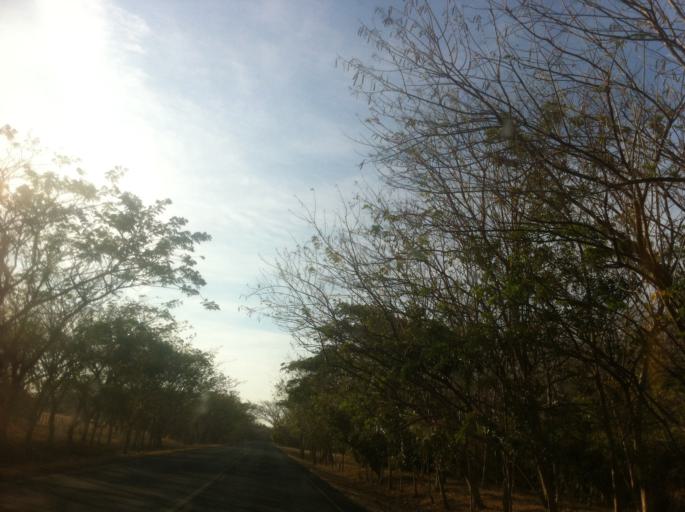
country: NI
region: Rivas
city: San Jorge
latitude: 11.3226
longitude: -85.7135
